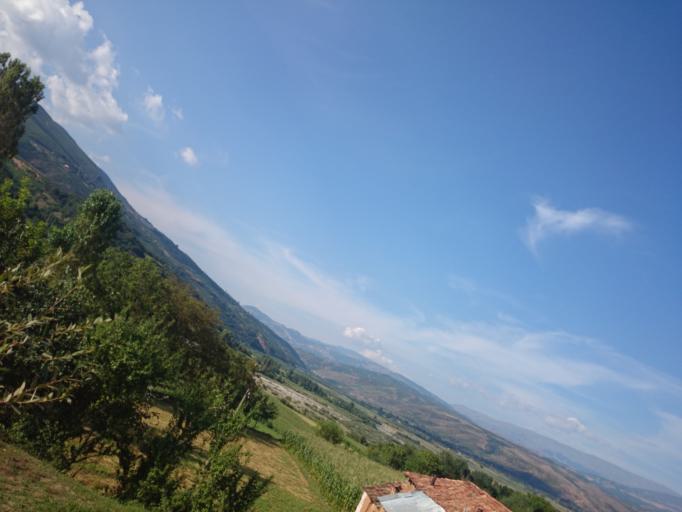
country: AL
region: Diber
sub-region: Rrethi i Dibres
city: Arras
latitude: 41.7349
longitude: 20.3166
